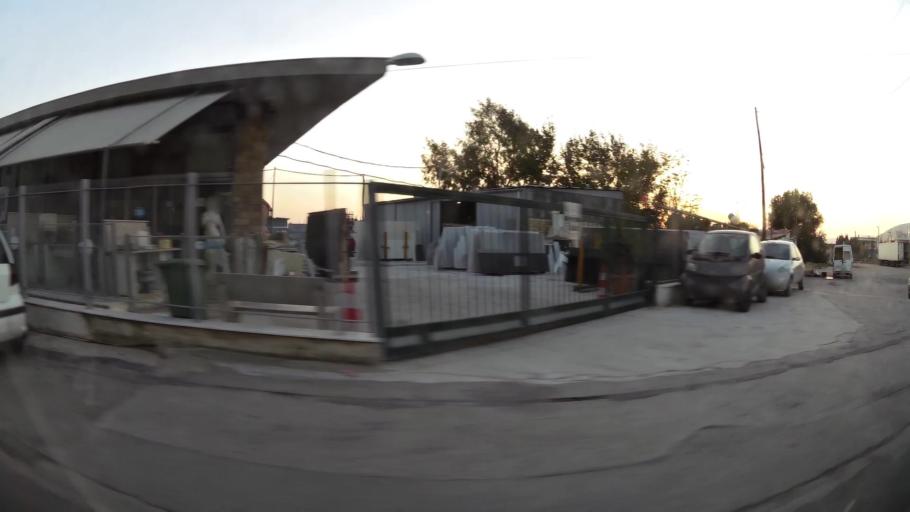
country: GR
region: Attica
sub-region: Nomarchia Anatolikis Attikis
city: Acharnes
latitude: 38.0933
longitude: 23.7535
